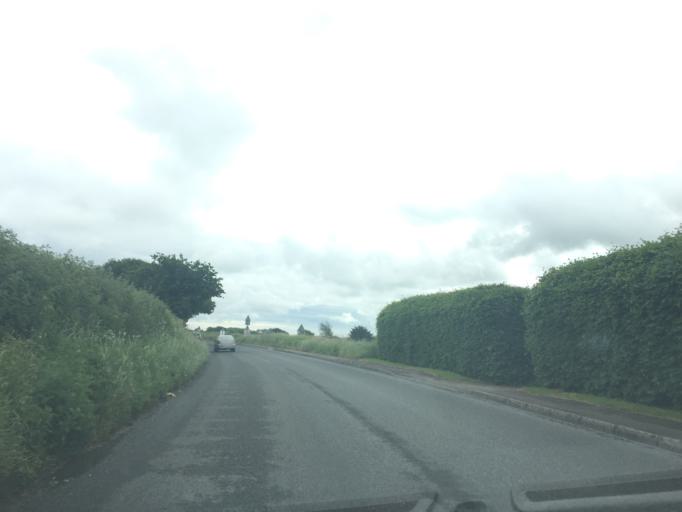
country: GB
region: England
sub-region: Dorset
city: Wool
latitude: 50.6832
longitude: -2.1816
